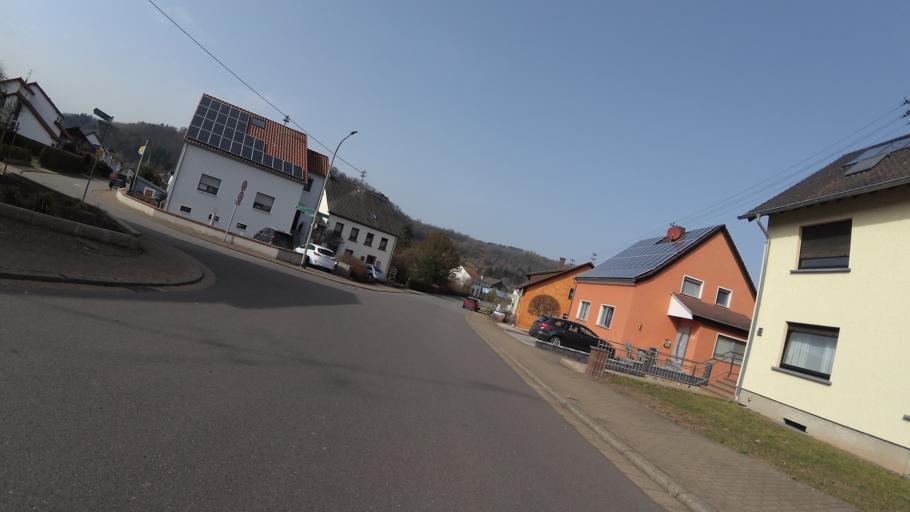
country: DE
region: Saarland
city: Beckingen
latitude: 49.4110
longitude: 6.7264
